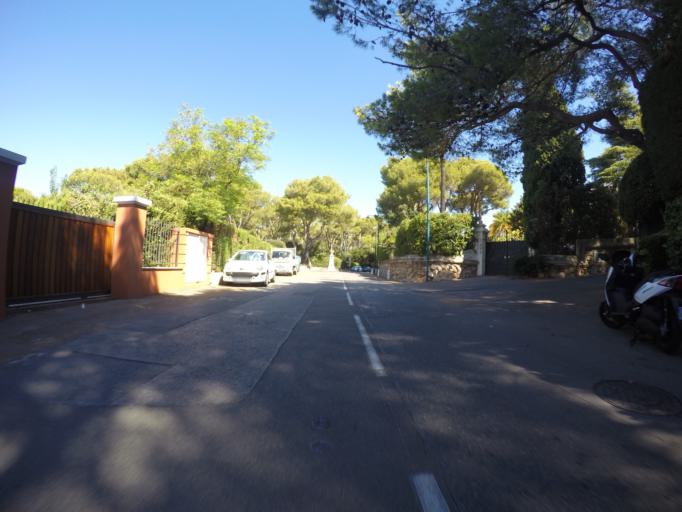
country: FR
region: Provence-Alpes-Cote d'Azur
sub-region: Departement des Alpes-Maritimes
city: Saint-Jean-Cap-Ferrat
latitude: 43.6877
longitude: 7.3241
